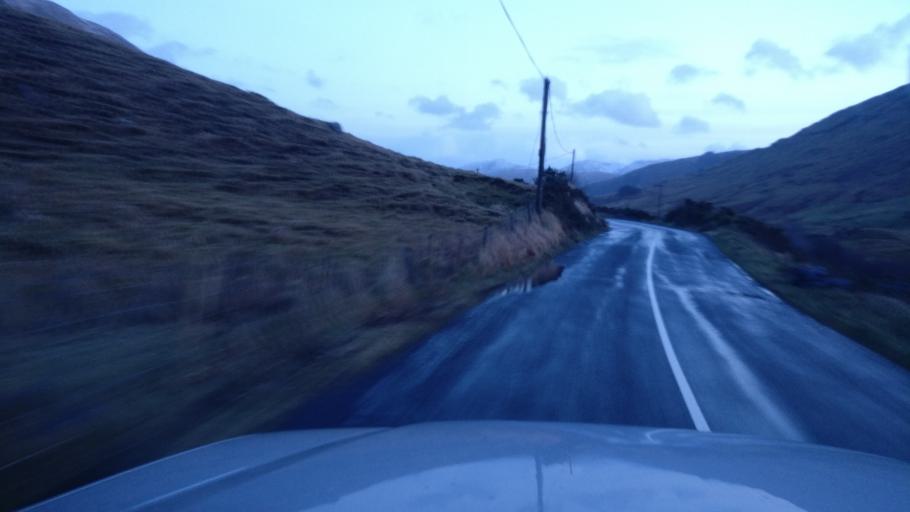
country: IE
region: Connaught
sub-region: Maigh Eo
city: Westport
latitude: 53.5735
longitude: -9.6619
